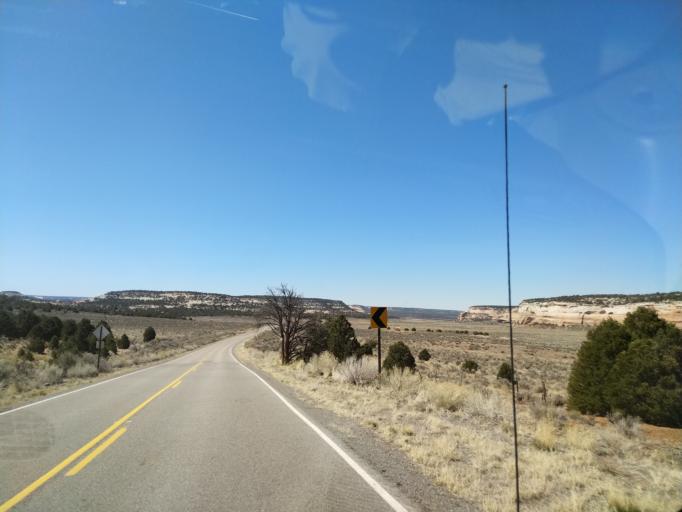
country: US
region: Colorado
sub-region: Mesa County
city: Fruita
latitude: 39.0031
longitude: -108.8470
